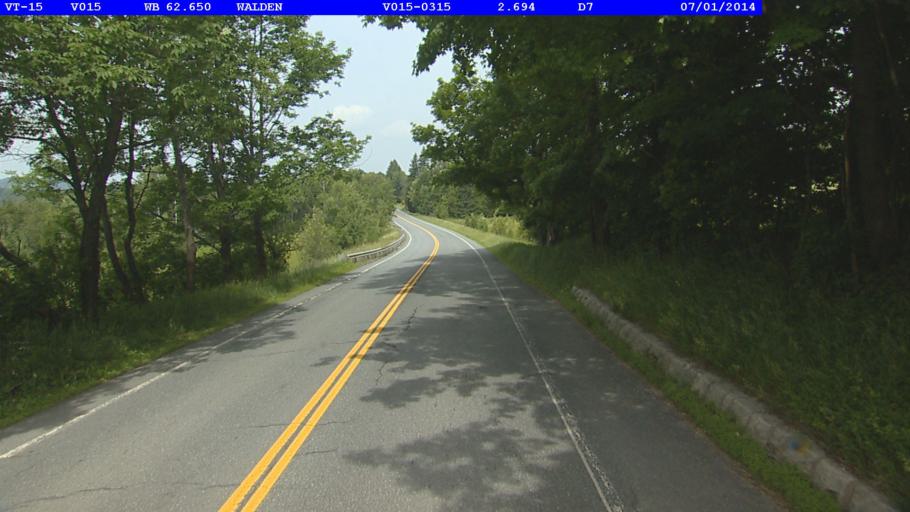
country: US
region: Vermont
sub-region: Caledonia County
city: Hardwick
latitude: 44.4613
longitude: -72.2643
